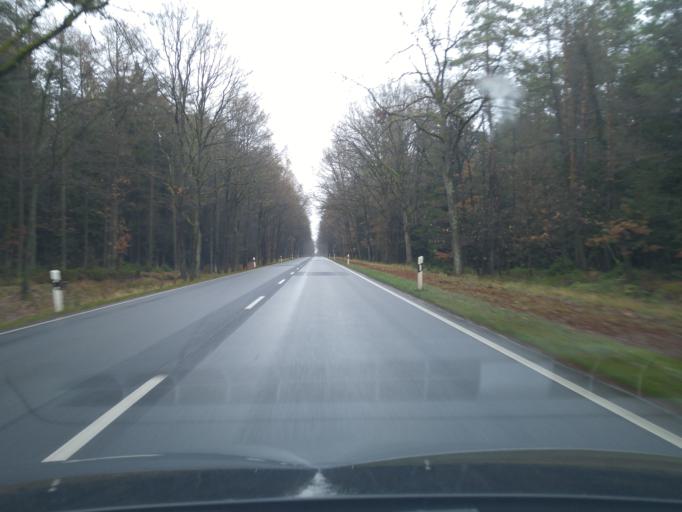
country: DE
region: Lower Saxony
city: Sprakensehl
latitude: 52.7410
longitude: 10.4878
